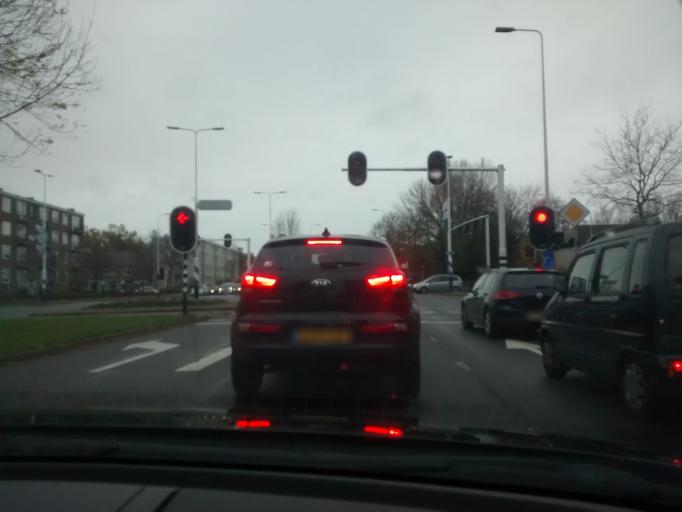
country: NL
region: South Holland
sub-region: Gemeente Leiden
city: Leiden
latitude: 52.1469
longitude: 4.4754
